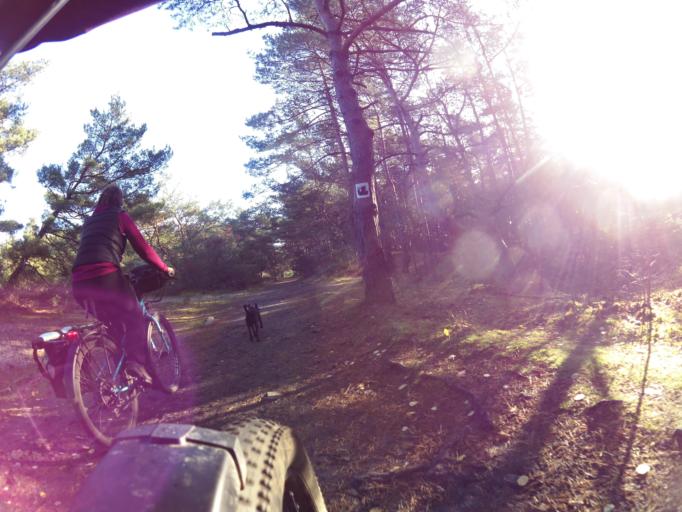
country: PL
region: Pomeranian Voivodeship
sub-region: Powiat pucki
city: Hel
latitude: 54.6048
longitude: 18.8199
